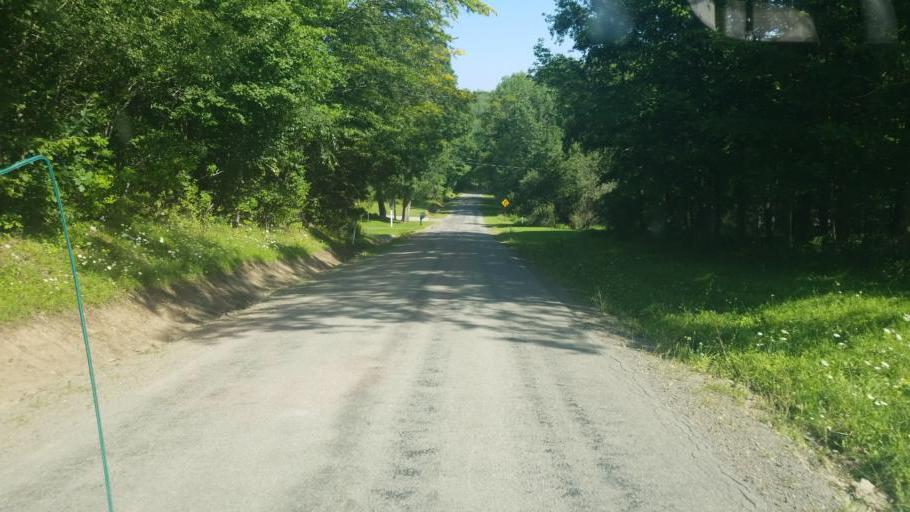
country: US
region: New York
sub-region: Allegany County
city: Bolivar
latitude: 42.0649
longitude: -78.0517
